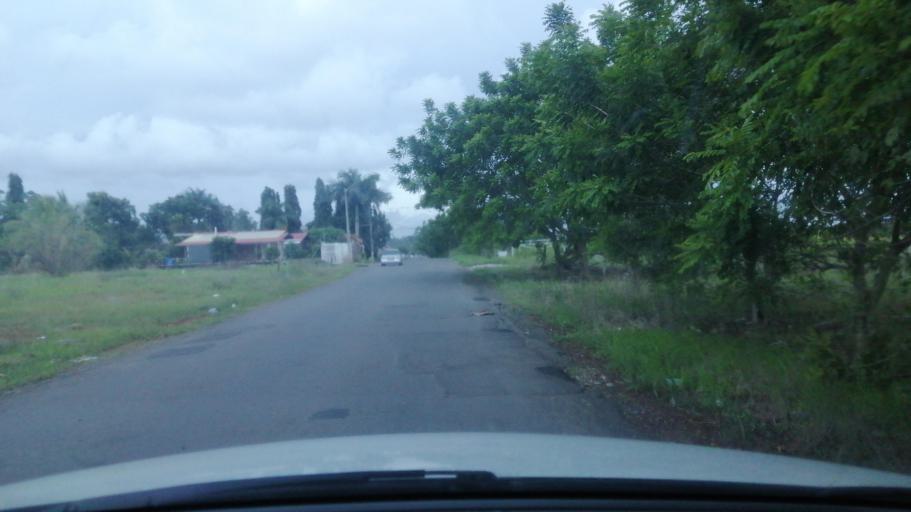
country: PA
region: Chiriqui
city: David
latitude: 8.4052
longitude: -82.4521
